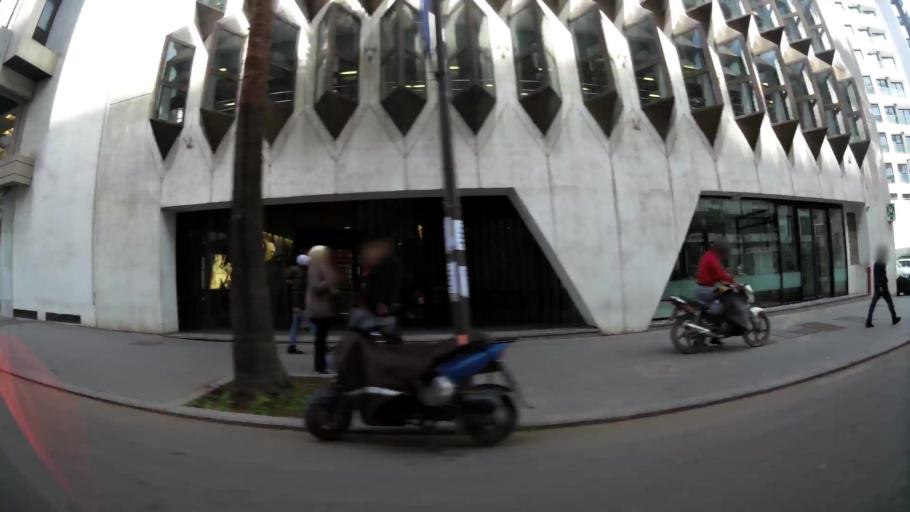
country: MA
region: Grand Casablanca
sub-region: Casablanca
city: Casablanca
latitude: 33.5852
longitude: -7.6226
